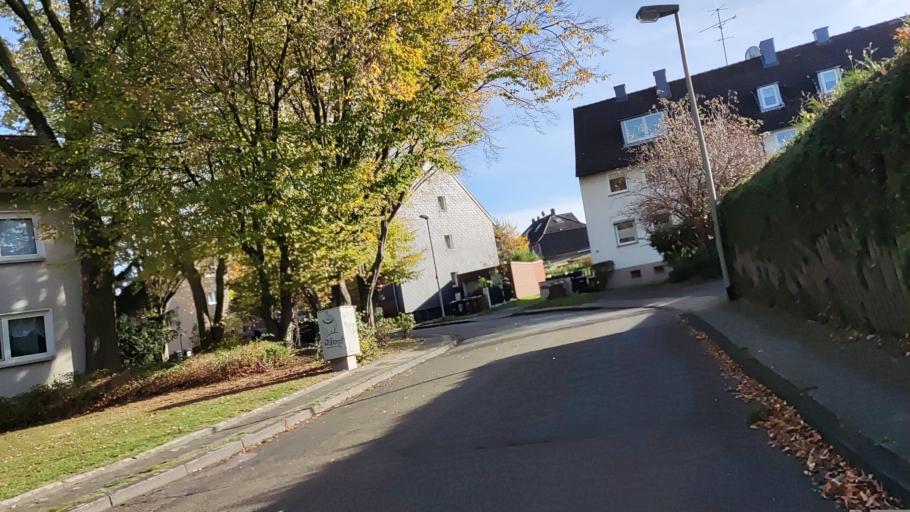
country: DE
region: North Rhine-Westphalia
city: Bochum-Hordel
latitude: 51.5223
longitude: 7.1834
